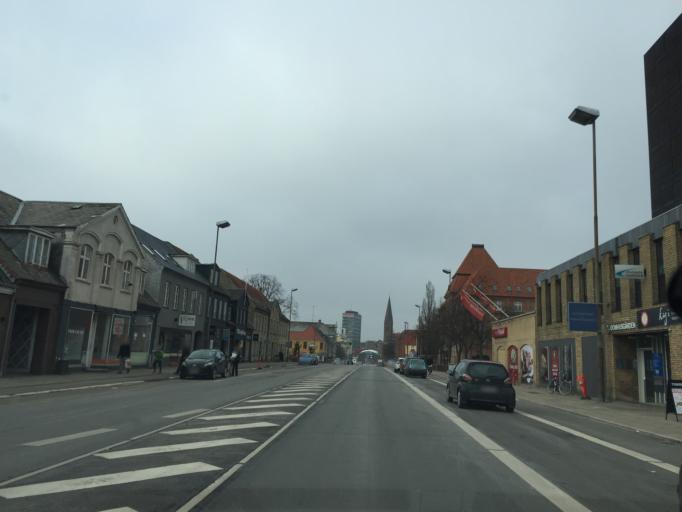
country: DK
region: South Denmark
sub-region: Odense Kommune
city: Odense
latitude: 55.3931
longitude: 10.3960
